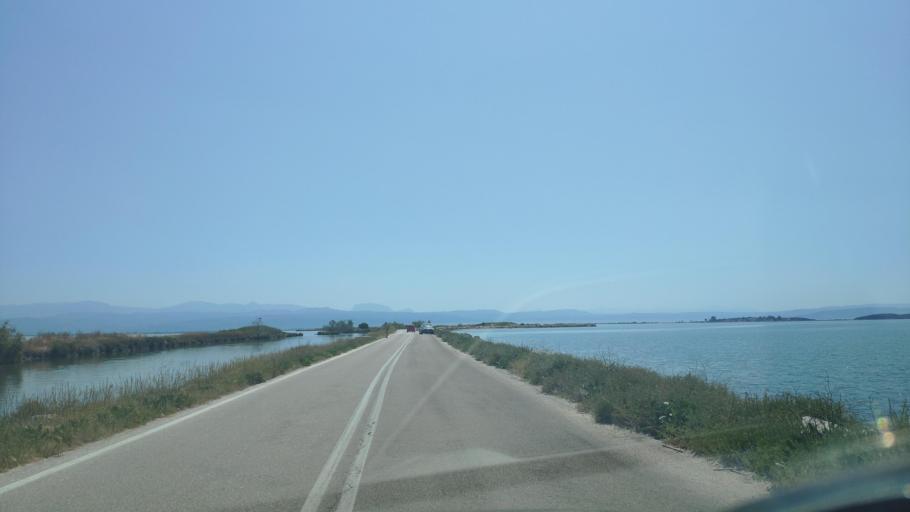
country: GR
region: Epirus
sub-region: Nomos Artas
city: Aneza
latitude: 39.0352
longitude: 20.8794
